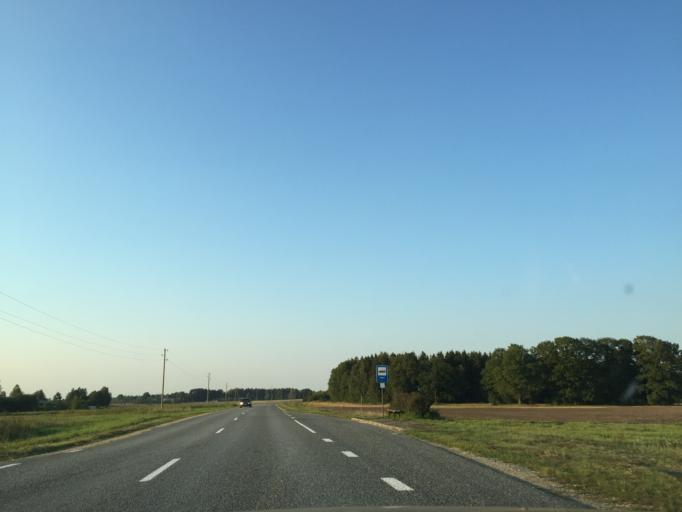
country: LV
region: Limbazu Rajons
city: Limbazi
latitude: 57.5745
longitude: 24.7712
